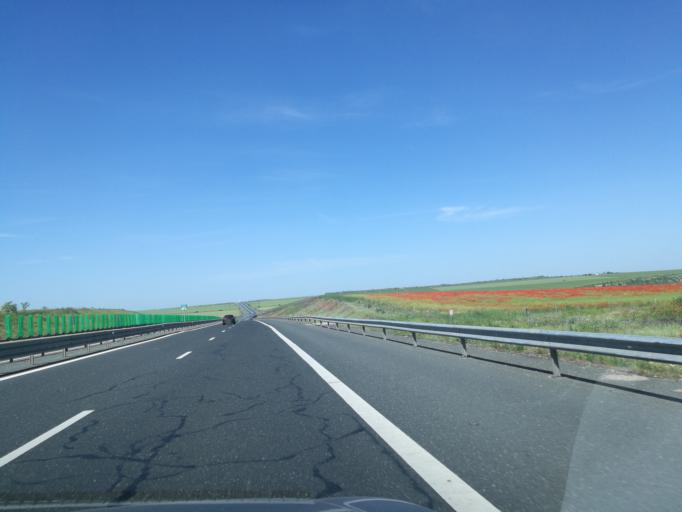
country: RO
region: Constanta
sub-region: Comuna Valu lui Traian
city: Valu lui Traian
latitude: 44.1395
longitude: 28.4517
